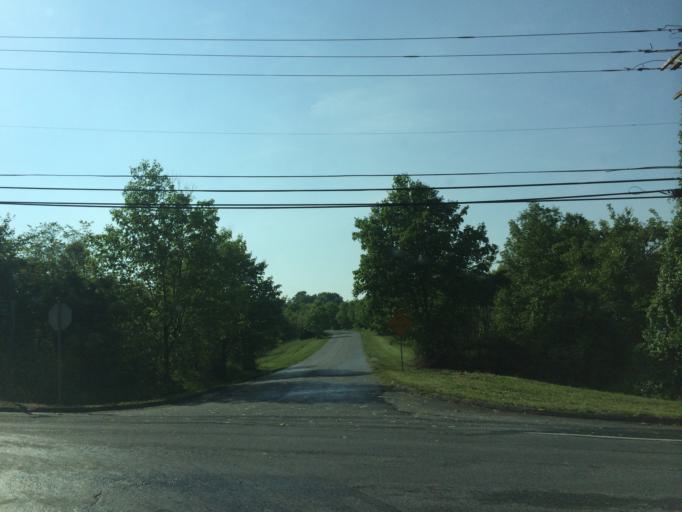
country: US
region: Maryland
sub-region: Howard County
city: Fulton
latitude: 39.1704
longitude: -76.9169
